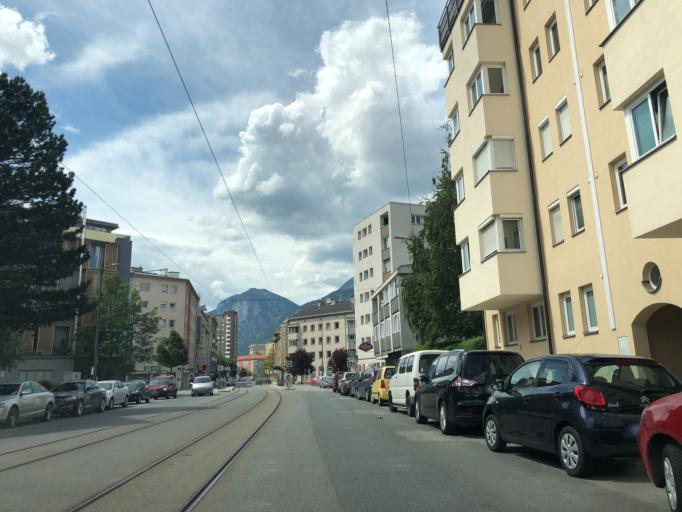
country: AT
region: Tyrol
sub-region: Innsbruck Stadt
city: Innsbruck
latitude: 47.2623
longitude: 11.4145
